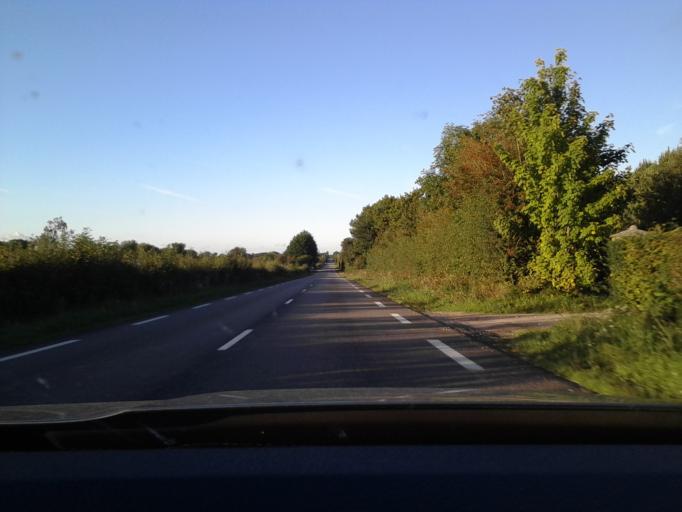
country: FR
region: Lower Normandy
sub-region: Departement de la Manche
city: Saint-Sauveur-le-Vicomte
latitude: 49.4037
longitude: -1.5118
